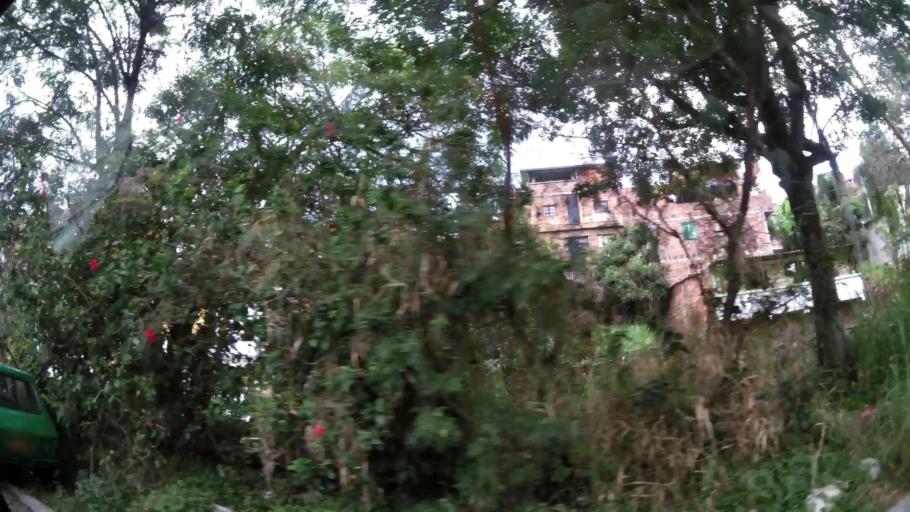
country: CO
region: Antioquia
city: Medellin
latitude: 6.2338
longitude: -75.5401
